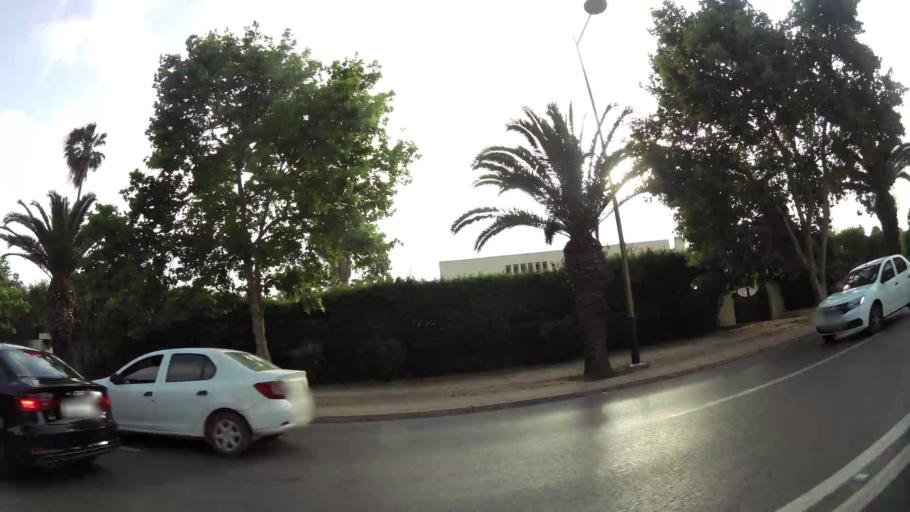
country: MA
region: Rabat-Sale-Zemmour-Zaer
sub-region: Rabat
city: Rabat
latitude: 33.9552
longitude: -6.8250
